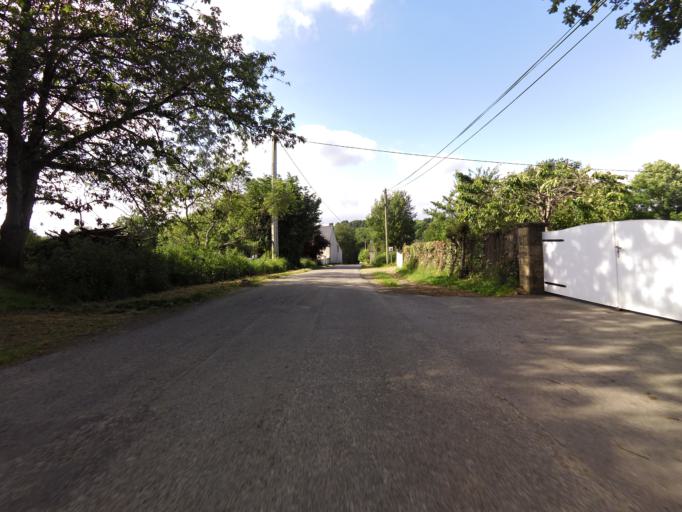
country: FR
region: Brittany
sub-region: Departement du Morbihan
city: Molac
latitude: 47.7157
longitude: -2.4140
